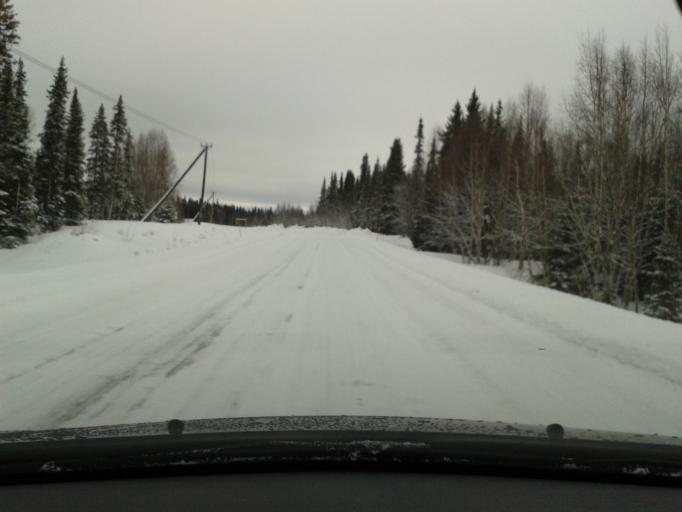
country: SE
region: Vaesterbotten
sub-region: Vilhelmina Kommun
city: Sjoberg
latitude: 65.2247
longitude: 15.9399
